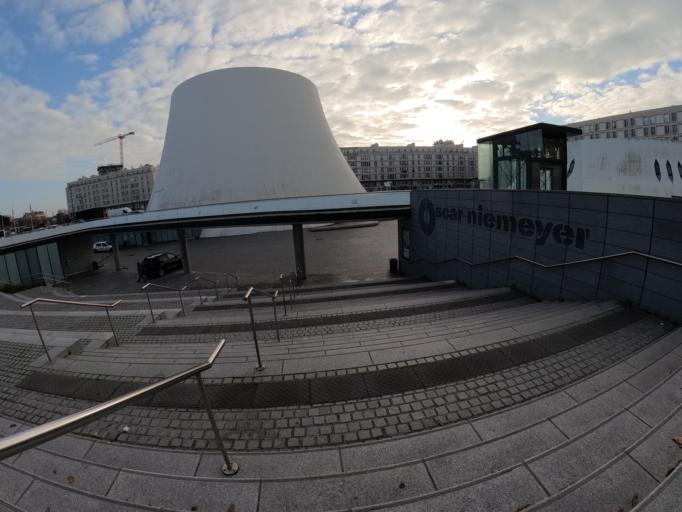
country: FR
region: Haute-Normandie
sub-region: Departement de la Seine-Maritime
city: Le Havre
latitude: 49.4909
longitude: 0.1067
